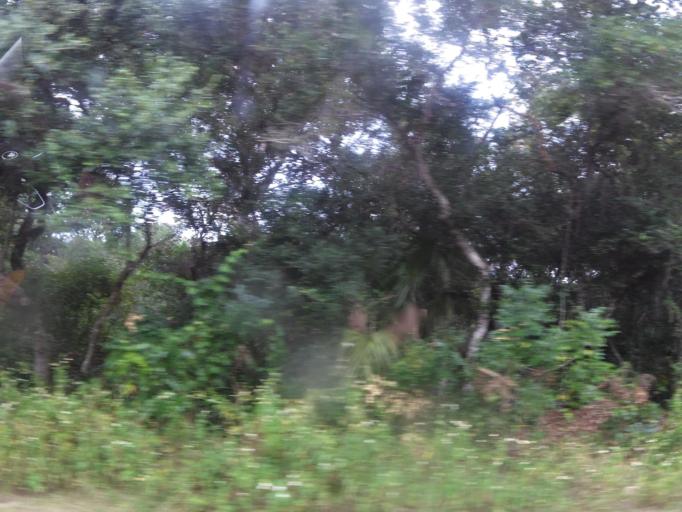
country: US
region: Florida
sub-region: Saint Johns County
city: Saint Augustine Beach
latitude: 29.8754
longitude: -81.2786
